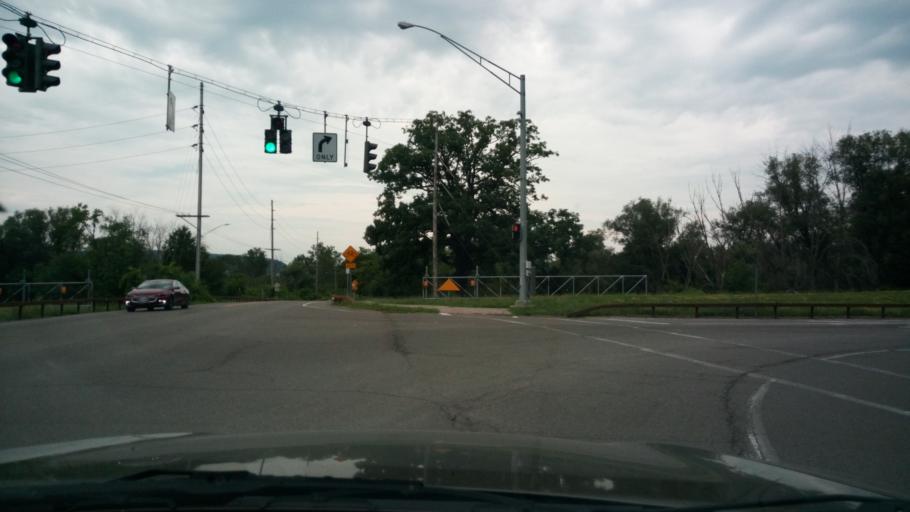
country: US
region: New York
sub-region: Chemung County
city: Elmira Heights
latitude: 42.1152
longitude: -76.8136
